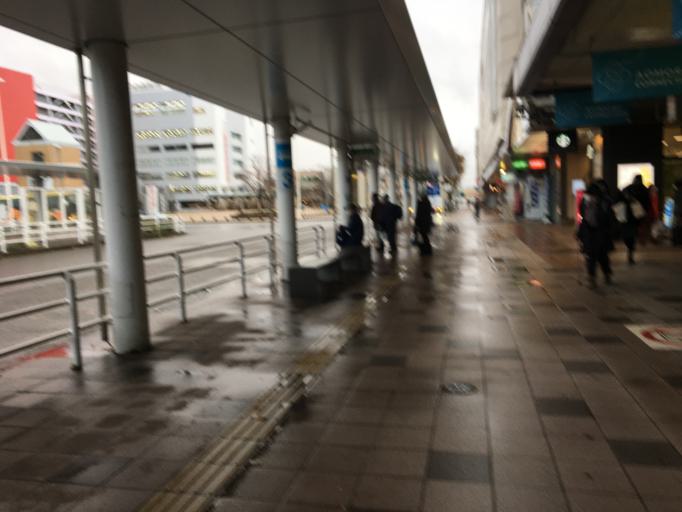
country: JP
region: Aomori
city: Aomori Shi
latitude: 40.8283
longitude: 140.7347
